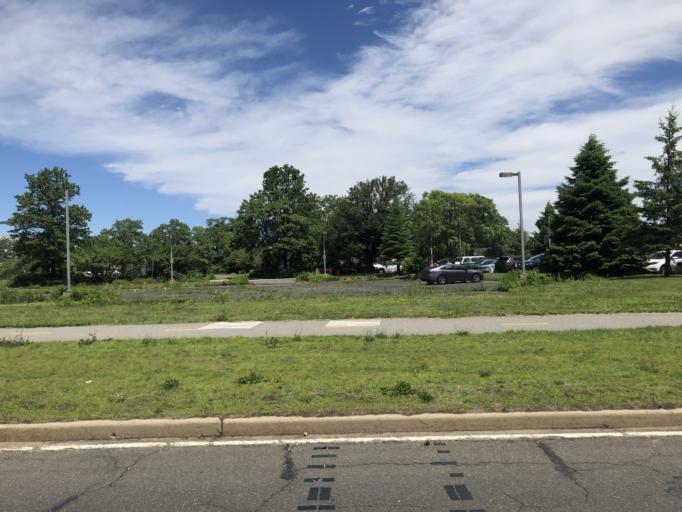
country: US
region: New York
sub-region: Nassau County
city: East Garden City
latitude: 40.7275
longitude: -73.6015
